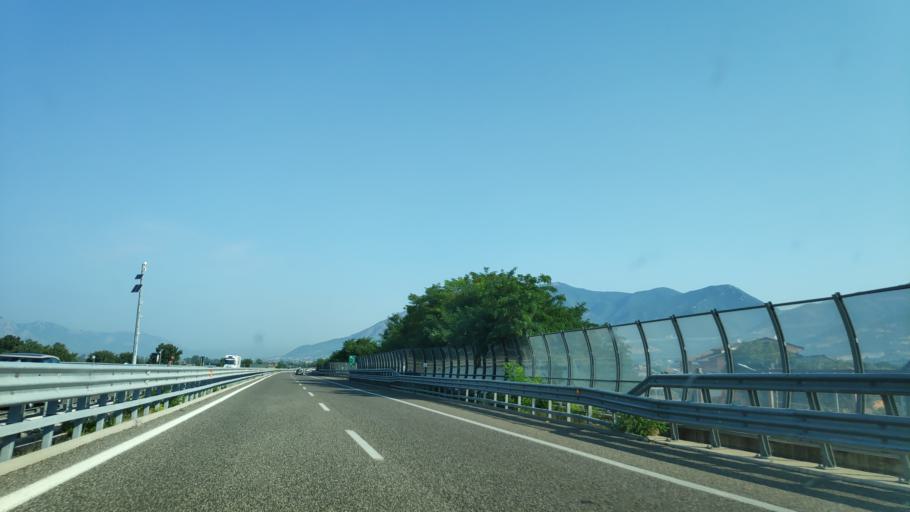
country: IT
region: Campania
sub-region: Provincia di Salerno
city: Padula
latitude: 40.3393
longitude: 15.6250
